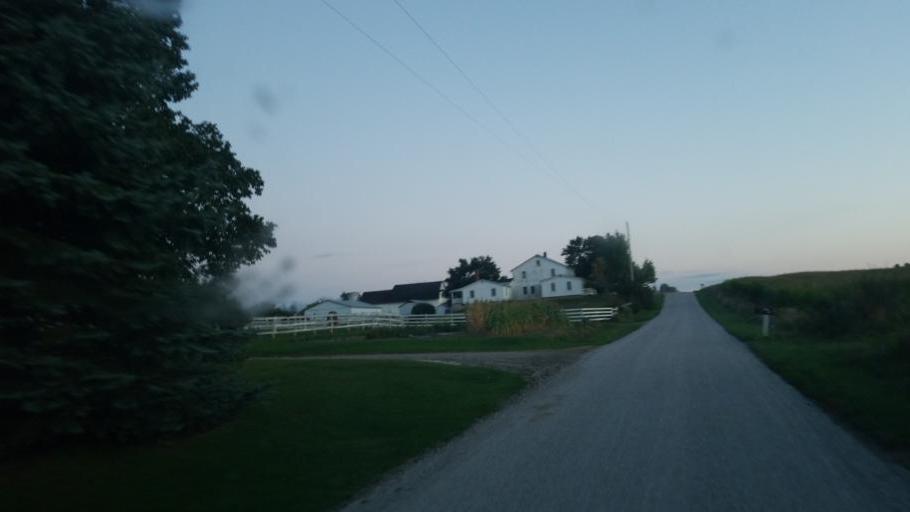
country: US
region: Ohio
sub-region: Ashland County
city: Ashland
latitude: 40.8779
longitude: -82.4067
